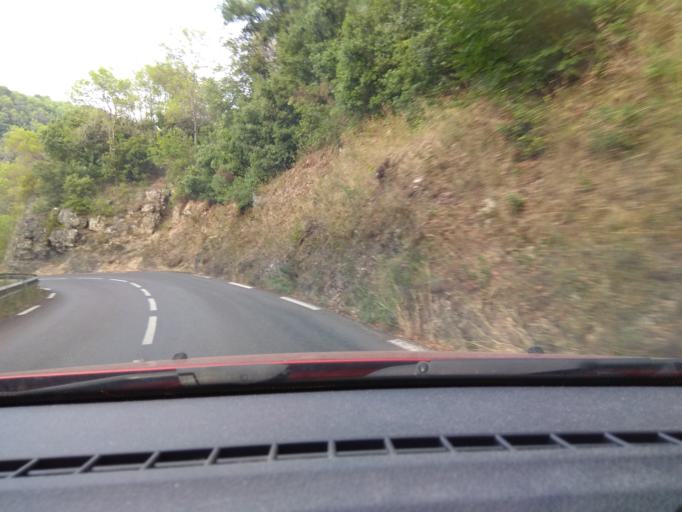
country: FR
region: Provence-Alpes-Cote d'Azur
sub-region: Departement des Alpes-Maritimes
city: Tourrettes-sur-Loup
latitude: 43.6877
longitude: 7.0676
